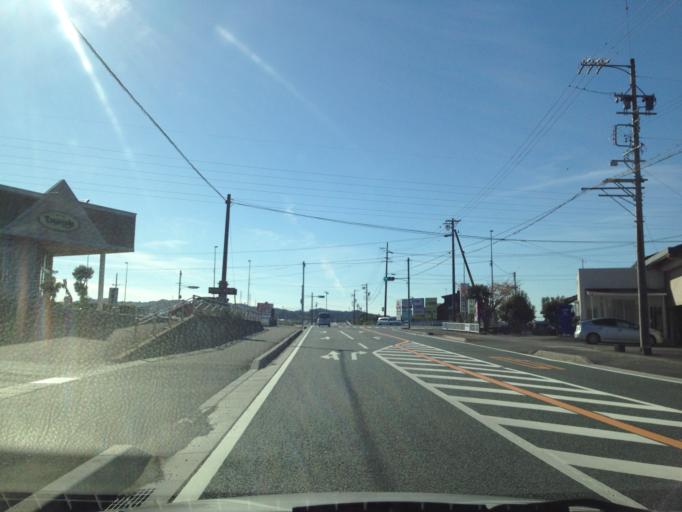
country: JP
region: Shizuoka
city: Kakegawa
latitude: 34.7607
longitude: 137.9726
